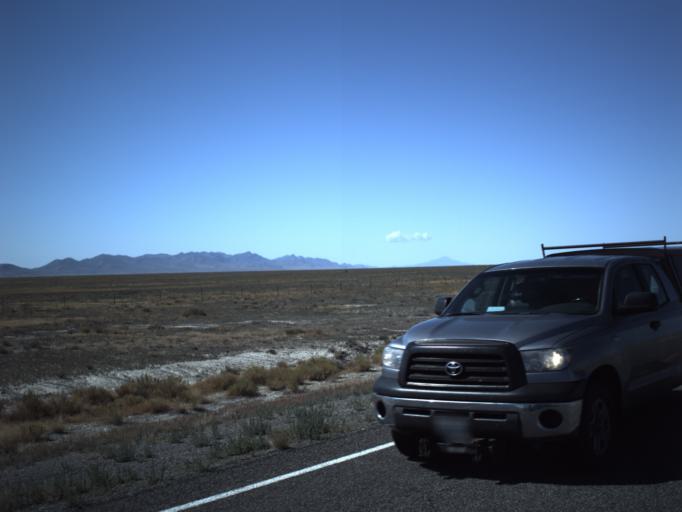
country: US
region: Utah
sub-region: Millard County
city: Delta
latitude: 39.2428
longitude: -112.9105
